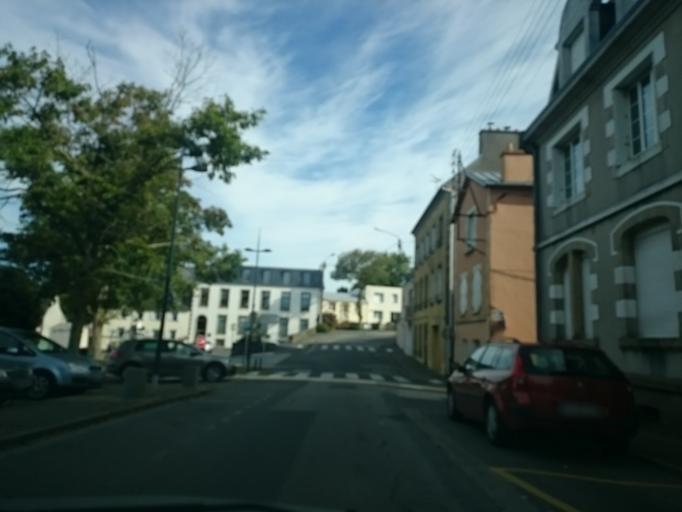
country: FR
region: Brittany
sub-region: Departement du Finistere
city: Brest
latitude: 48.4164
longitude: -4.4923
